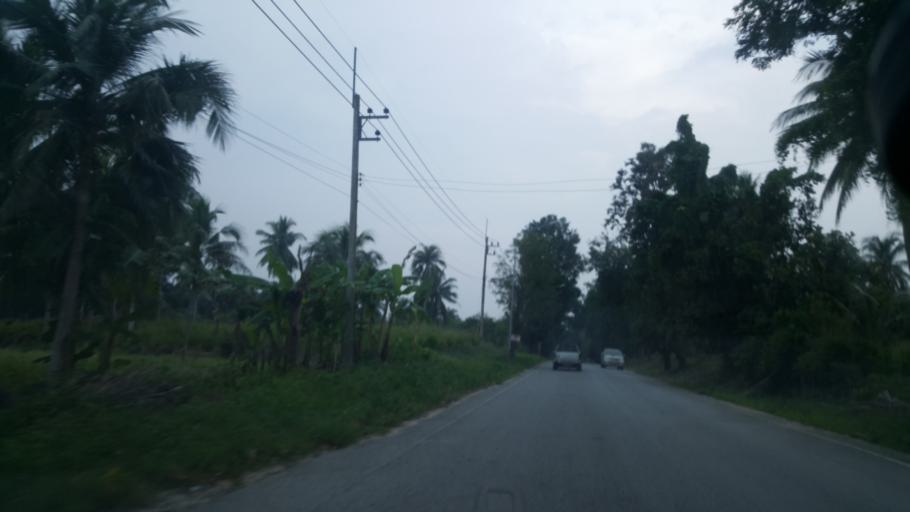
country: TH
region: Chon Buri
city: Si Racha
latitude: 13.2368
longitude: 101.0238
